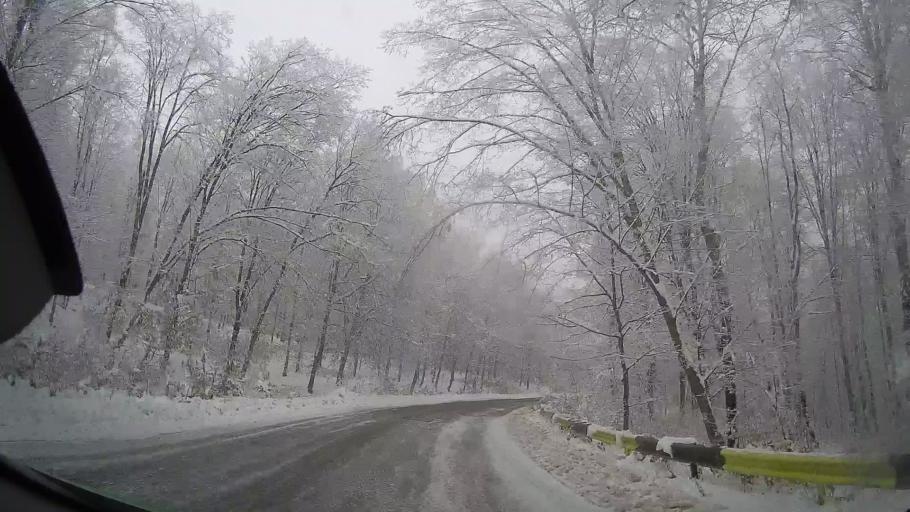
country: RO
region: Neamt
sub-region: Comuna Valea Ursului
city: Valea Ursului
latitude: 46.8391
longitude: 27.0690
